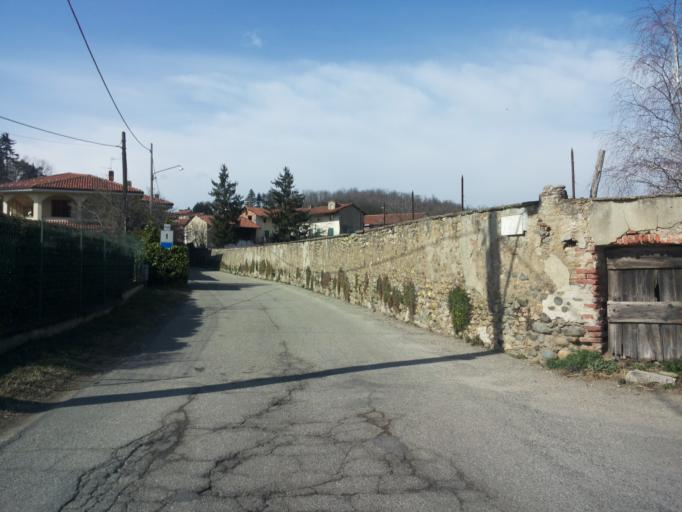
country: IT
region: Piedmont
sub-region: Provincia di Torino
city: Maglione
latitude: 45.3446
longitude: 8.0159
